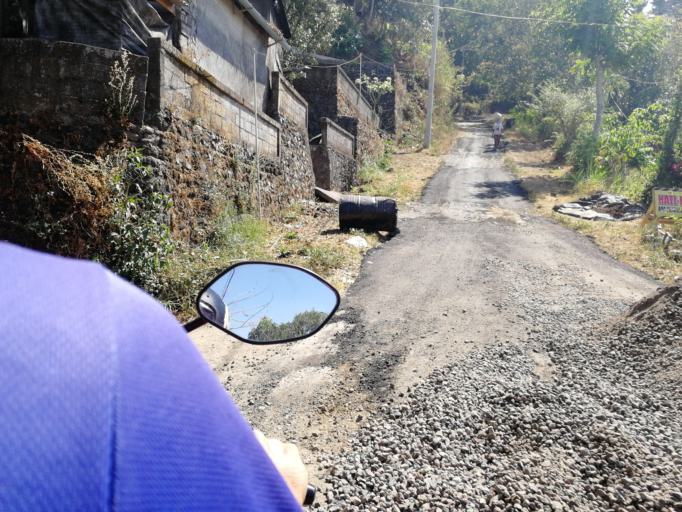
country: ID
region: Bali
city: Banjar Kedisan
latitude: -8.1682
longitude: 115.3017
